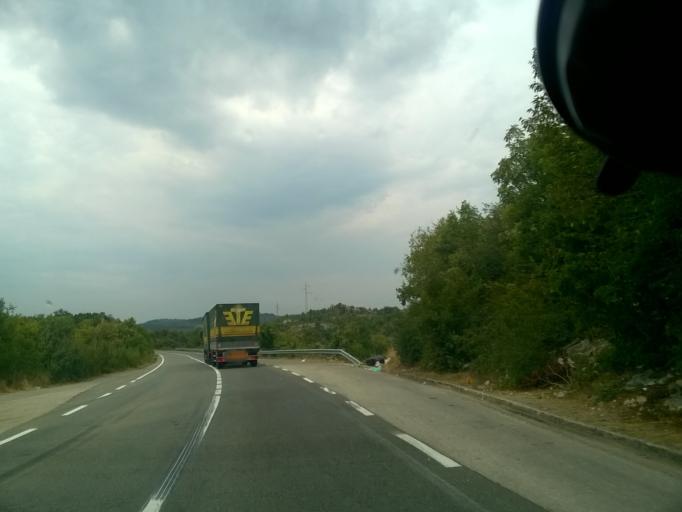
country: ME
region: Kotor
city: Risan
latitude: 42.7391
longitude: 18.6287
